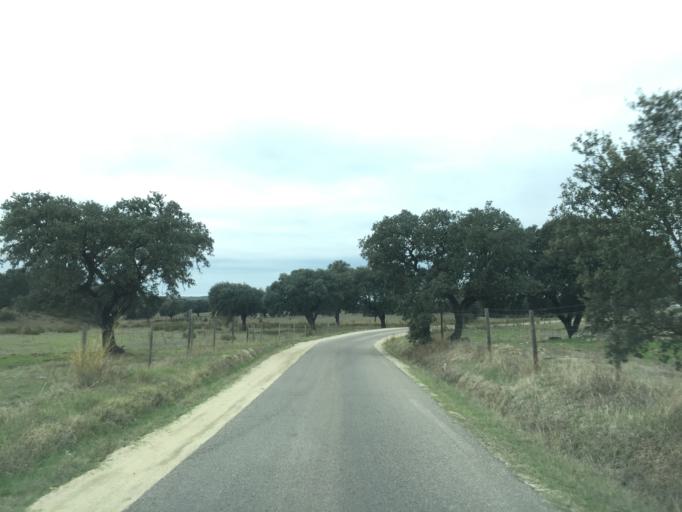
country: PT
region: Portalegre
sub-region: Fronteira
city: Vale da Amoreira
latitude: 39.0497
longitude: -7.7893
